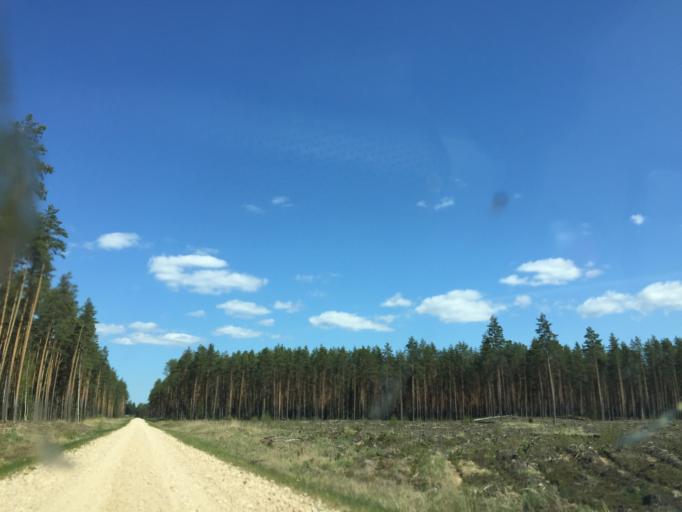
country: LV
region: Vecumnieki
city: Vecumnieki
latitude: 56.6523
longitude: 24.4852
